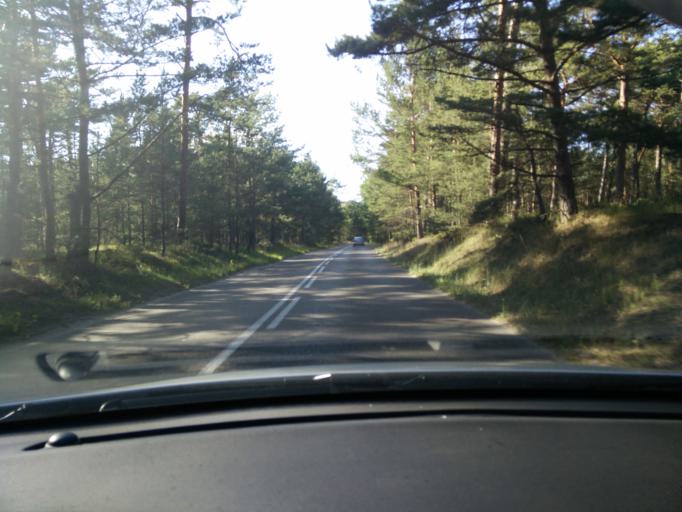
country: PL
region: Pomeranian Voivodeship
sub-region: Powiat pucki
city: Hel
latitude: 54.6237
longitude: 18.7959
